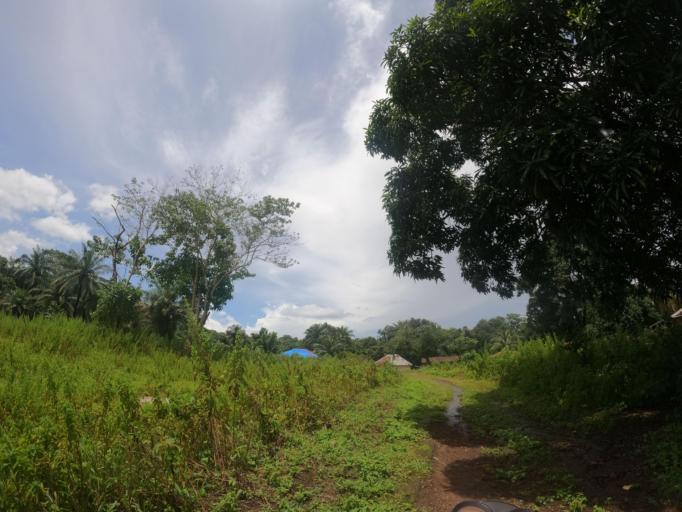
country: SL
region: Northern Province
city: Binkolo
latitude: 9.1610
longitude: -12.1904
